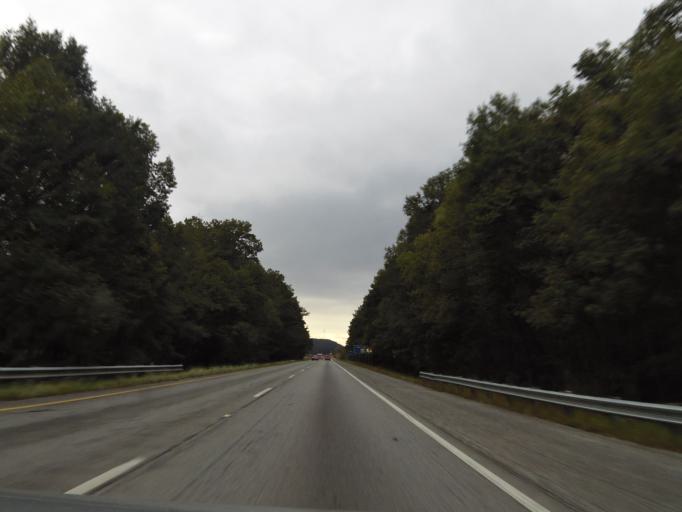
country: US
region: Alabama
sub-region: Saint Clair County
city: Springville
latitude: 33.7808
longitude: -86.4154
